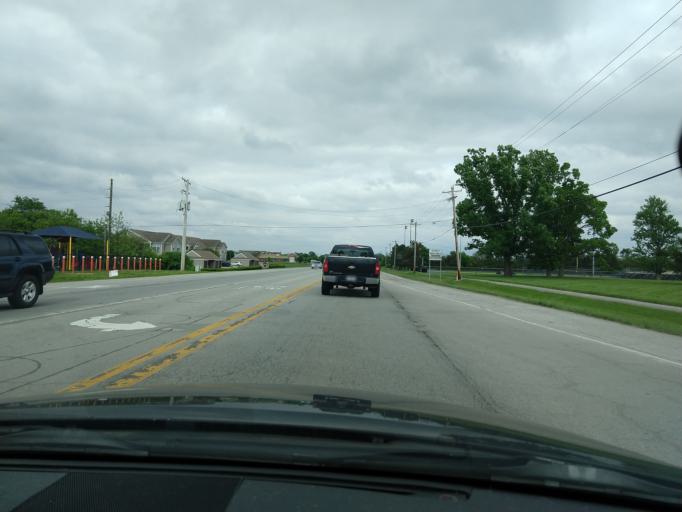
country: US
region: Indiana
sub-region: Hamilton County
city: Westfield
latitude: 40.0431
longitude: -86.0794
